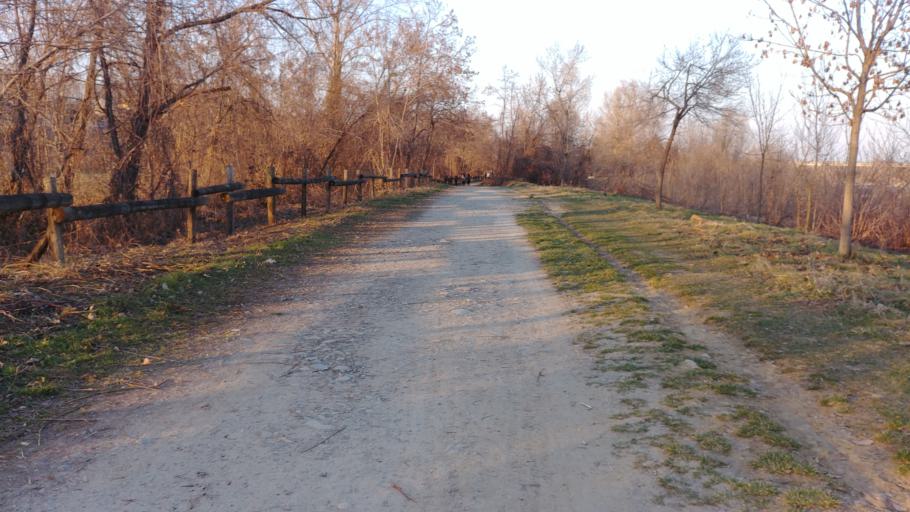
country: IT
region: Piedmont
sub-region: Provincia di Cuneo
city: Cuneo
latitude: 44.3637
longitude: 7.5387
